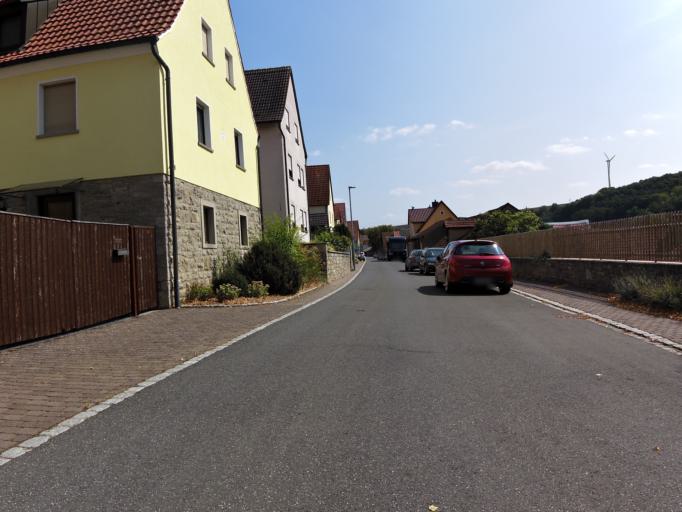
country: DE
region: Bavaria
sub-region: Regierungsbezirk Unterfranken
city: Theilheim
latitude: 49.7549
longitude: 10.0308
